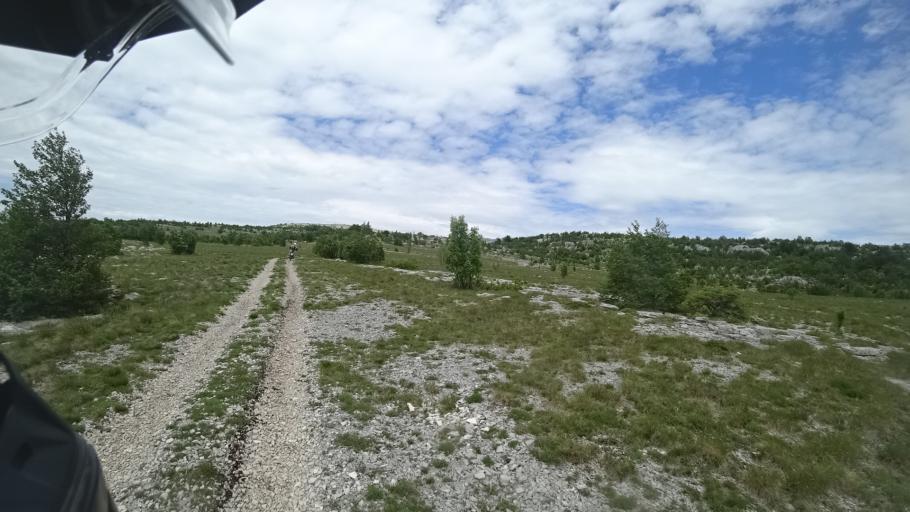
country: HR
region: Splitsko-Dalmatinska
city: Hrvace
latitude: 43.8874
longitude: 16.5886
